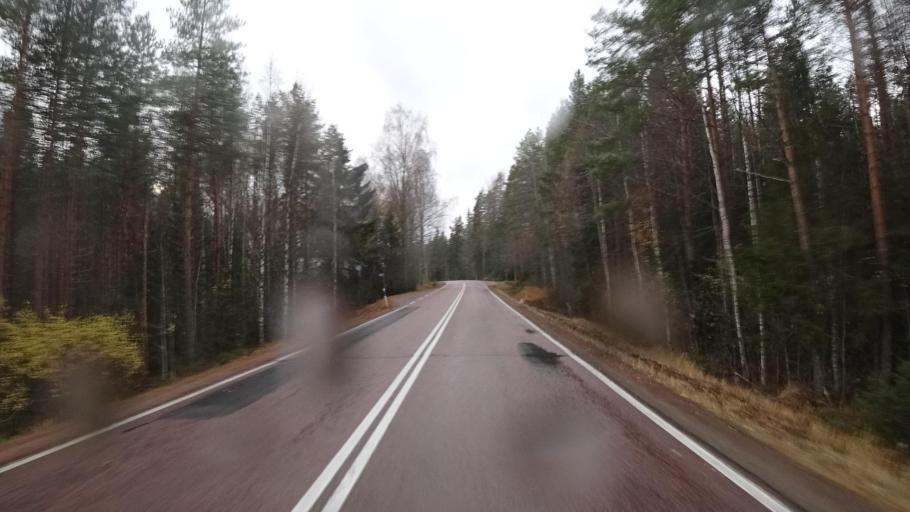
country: FI
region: Southern Savonia
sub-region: Mikkeli
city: Kangasniemi
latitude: 62.0715
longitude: 26.6732
